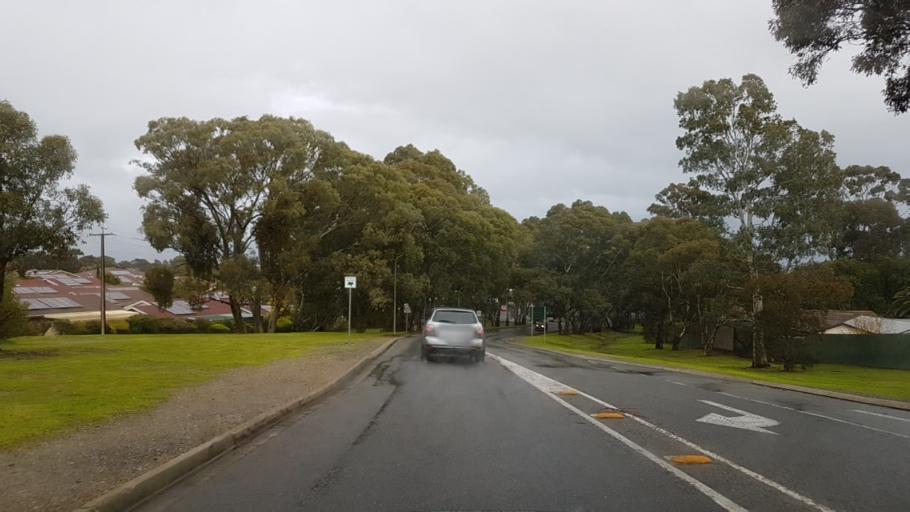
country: AU
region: South Australia
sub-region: Onkaparinga
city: Craigburn Farm
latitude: -35.0582
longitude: 138.6017
